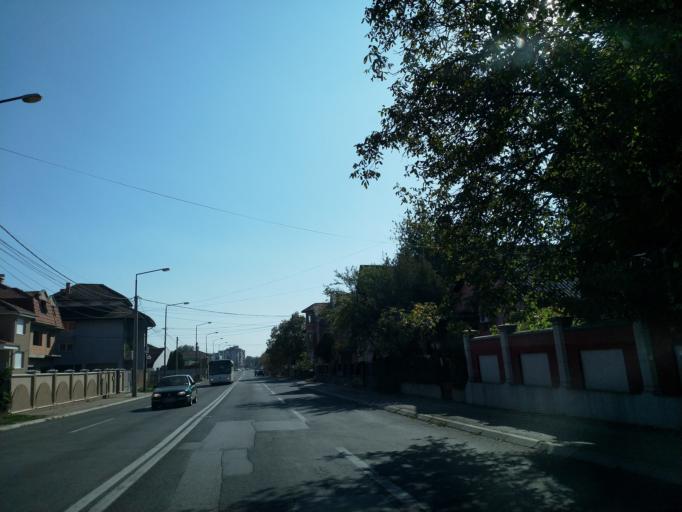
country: RS
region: Central Serbia
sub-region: Pomoravski Okrug
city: Paracin
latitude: 43.8648
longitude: 21.4207
